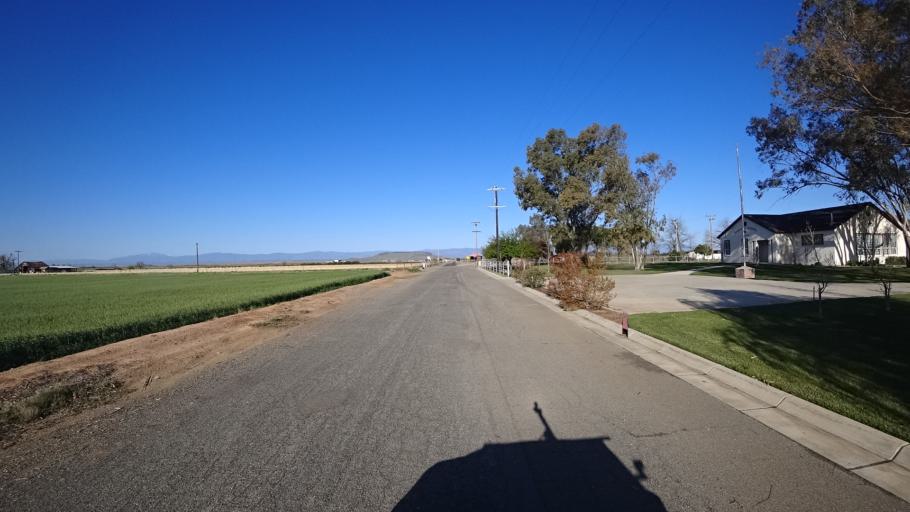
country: US
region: California
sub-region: Glenn County
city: Orland
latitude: 39.7589
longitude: -122.2468
